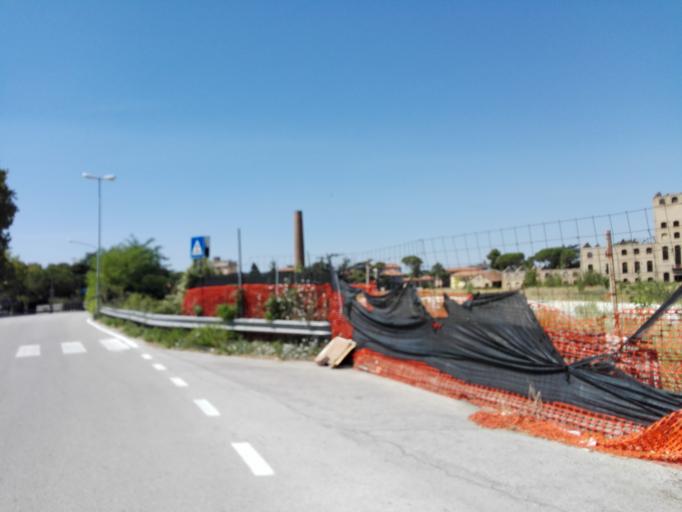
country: IT
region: Umbria
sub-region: Provincia di Perugia
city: Foligno
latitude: 42.9614
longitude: 12.7056
